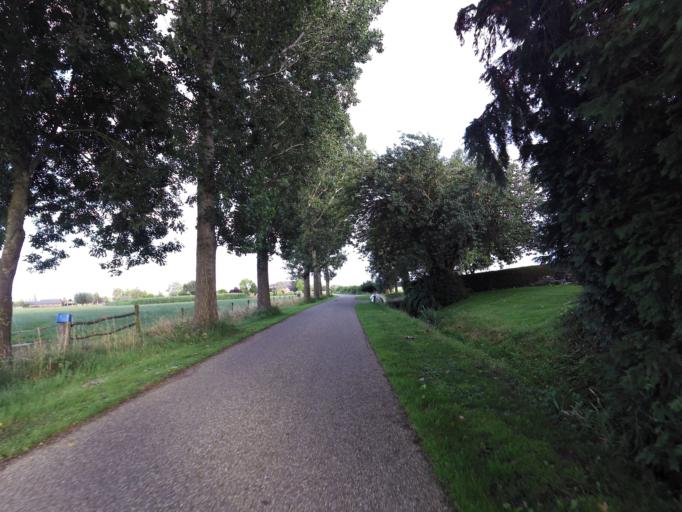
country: NL
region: Gelderland
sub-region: Gemeente Doesburg
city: Doesburg
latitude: 51.9769
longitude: 6.1997
